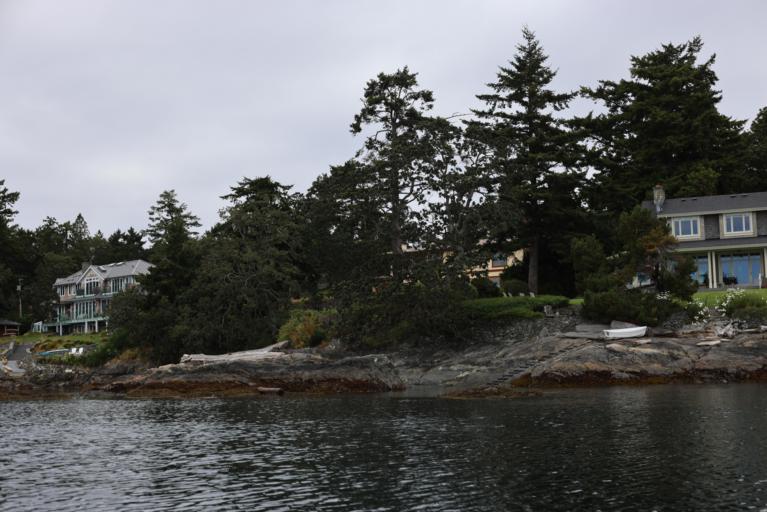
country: CA
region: British Columbia
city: Oak Bay
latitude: 48.4516
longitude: -123.2825
